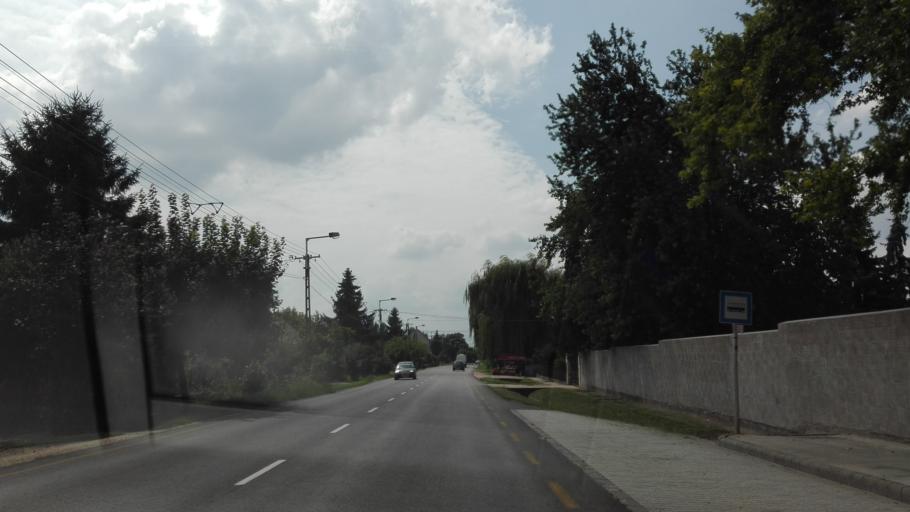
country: HU
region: Fejer
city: Cece
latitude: 46.7727
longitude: 18.6374
